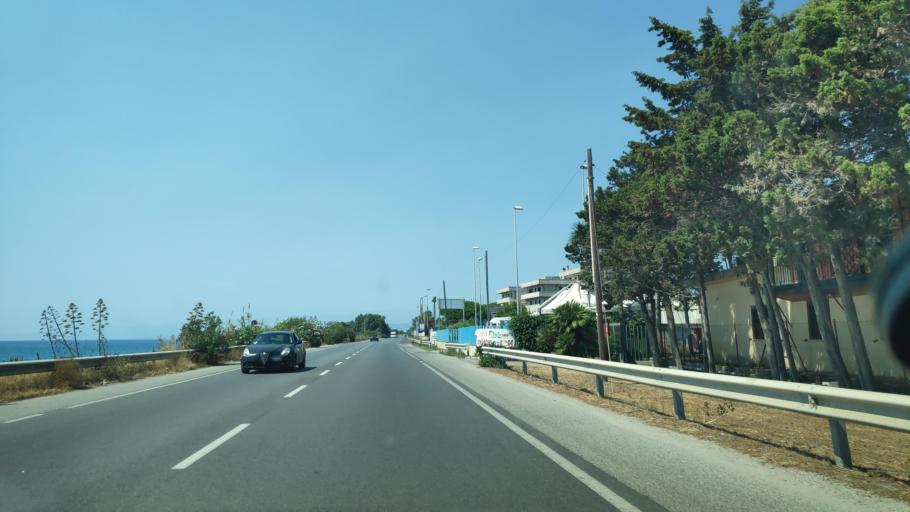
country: IT
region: Calabria
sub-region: Provincia di Reggio Calabria
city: Roccella Ionica
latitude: 38.3121
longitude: 16.3771
